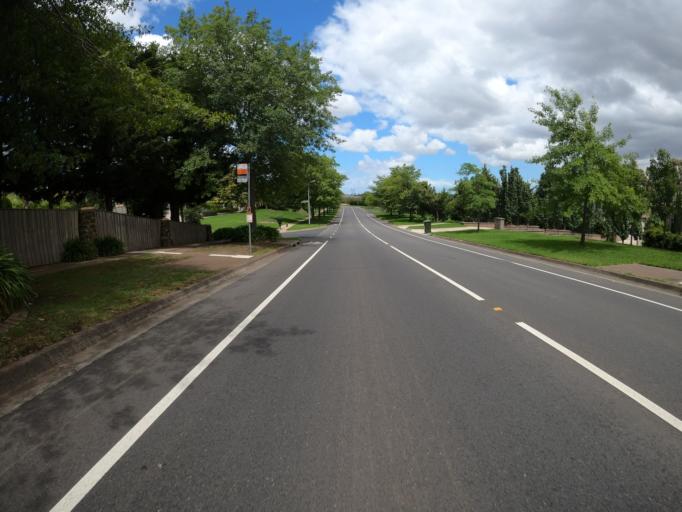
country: AU
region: Victoria
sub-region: Hume
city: Attwood
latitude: -37.6591
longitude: 144.8991
